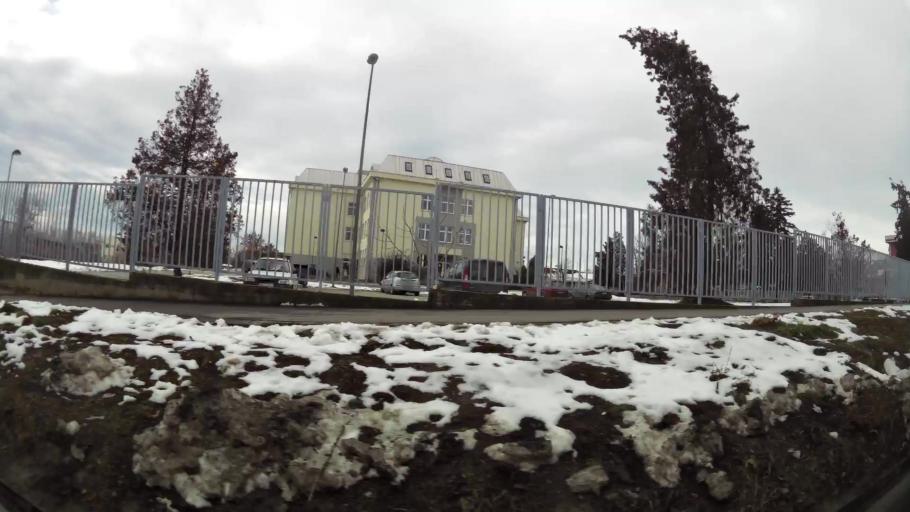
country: RS
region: Central Serbia
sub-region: Belgrade
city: Surcin
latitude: 44.7896
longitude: 20.2708
